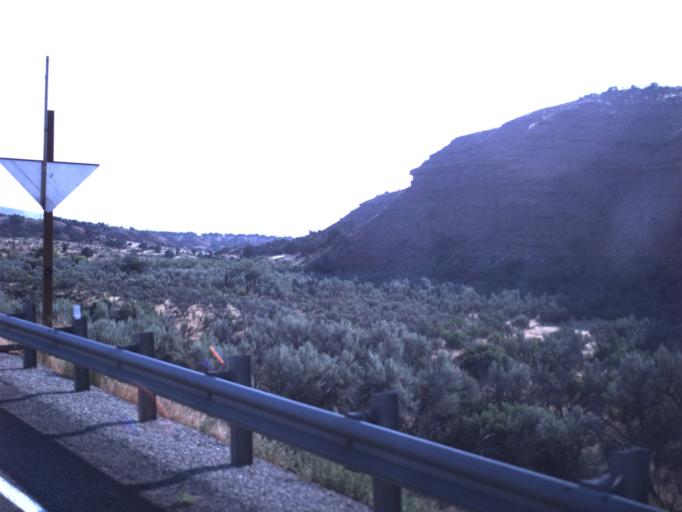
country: US
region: Utah
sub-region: Uintah County
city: Vernal
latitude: 40.5972
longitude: -109.4662
